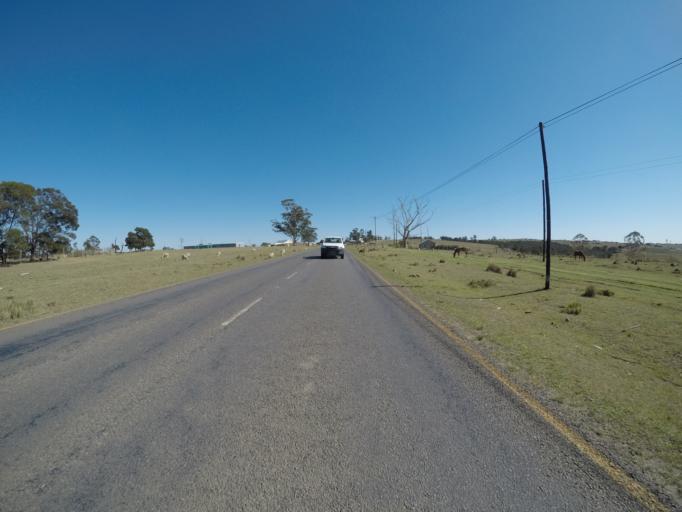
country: ZA
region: Eastern Cape
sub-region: OR Tambo District Municipality
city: Mthatha
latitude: -31.7985
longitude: 28.7456
